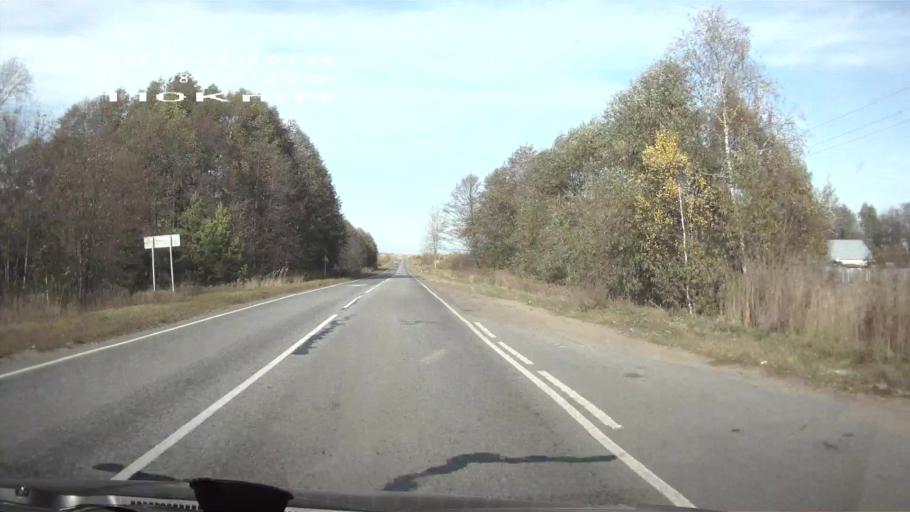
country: RU
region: Chuvashia
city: Ibresi
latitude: 55.2578
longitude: 47.0793
